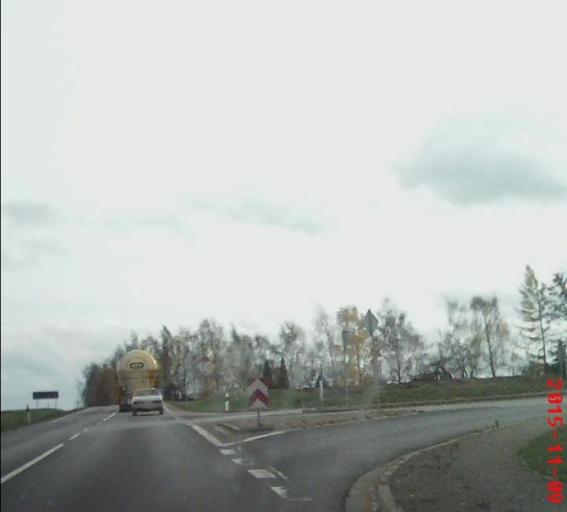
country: DE
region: Thuringia
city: Seebach
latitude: 51.1796
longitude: 10.5074
